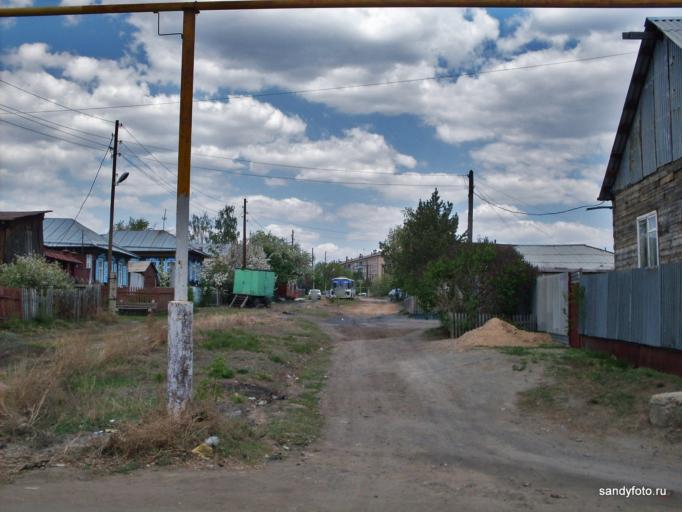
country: RU
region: Chelyabinsk
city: Troitsk
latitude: 54.1011
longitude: 61.5610
